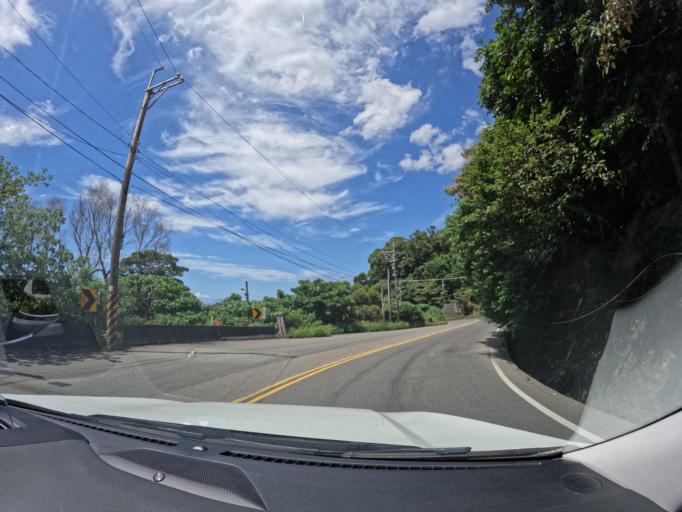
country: TW
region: Taipei
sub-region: Taipei
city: Banqiao
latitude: 25.1178
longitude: 121.3880
